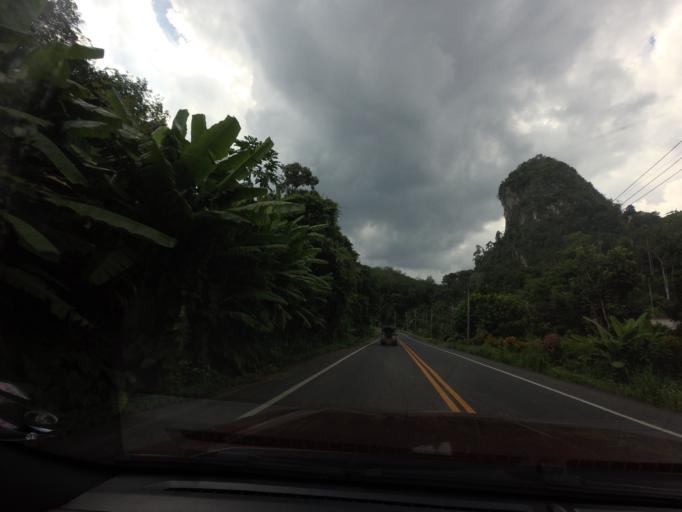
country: TH
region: Yala
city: Than To
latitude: 6.2081
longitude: 101.1688
